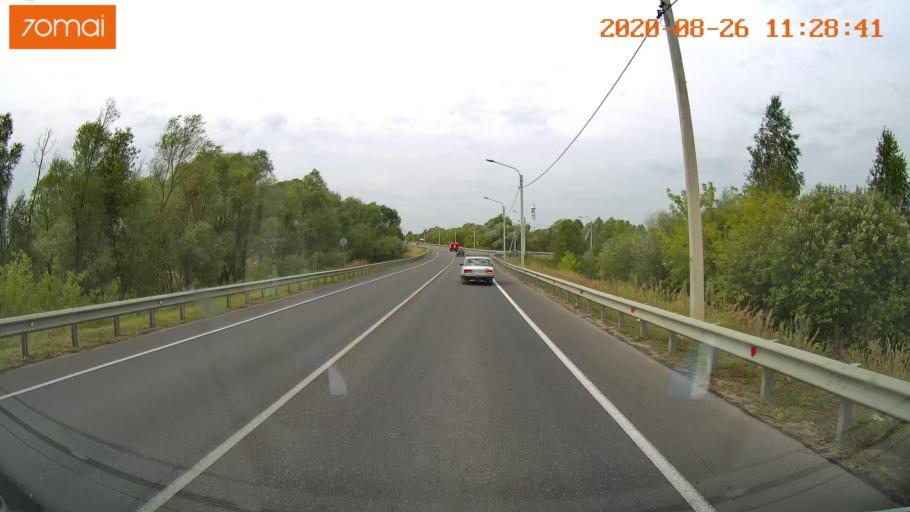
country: RU
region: Rjazan
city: Shilovo
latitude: 54.3232
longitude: 40.9079
